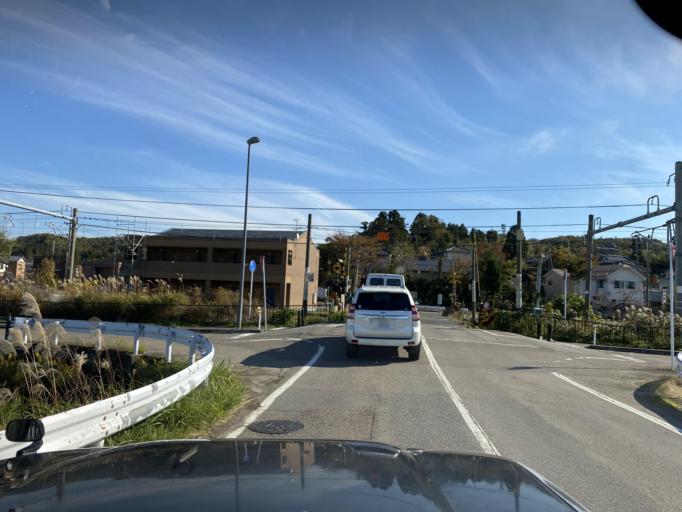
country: JP
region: Niigata
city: Niitsu-honcho
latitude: 37.7532
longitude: 139.0982
